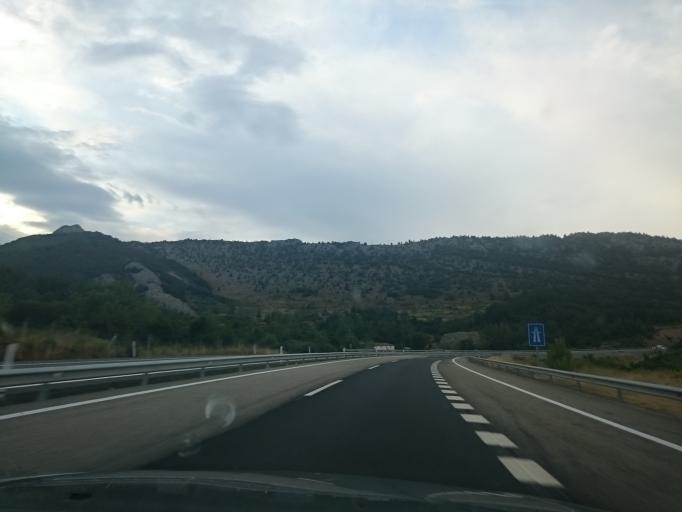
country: ES
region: Castille and Leon
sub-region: Provincia de Leon
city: Sena de Luna
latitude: 42.8693
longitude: -5.8853
